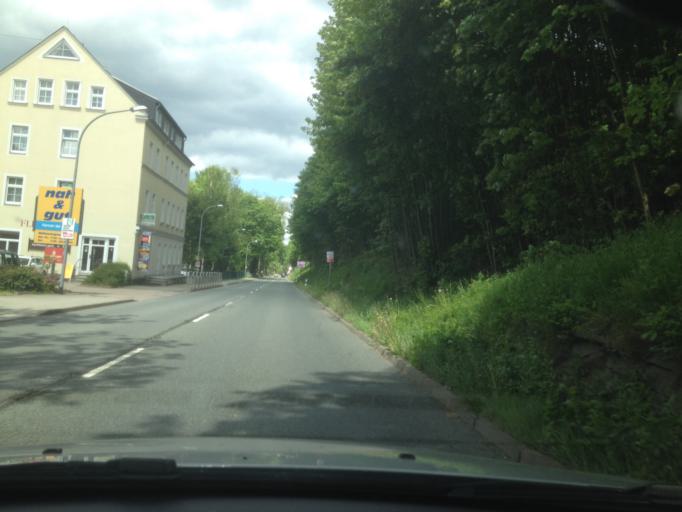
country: DE
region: Saxony
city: Annaberg-Buchholz
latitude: 50.5624
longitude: 12.9991
